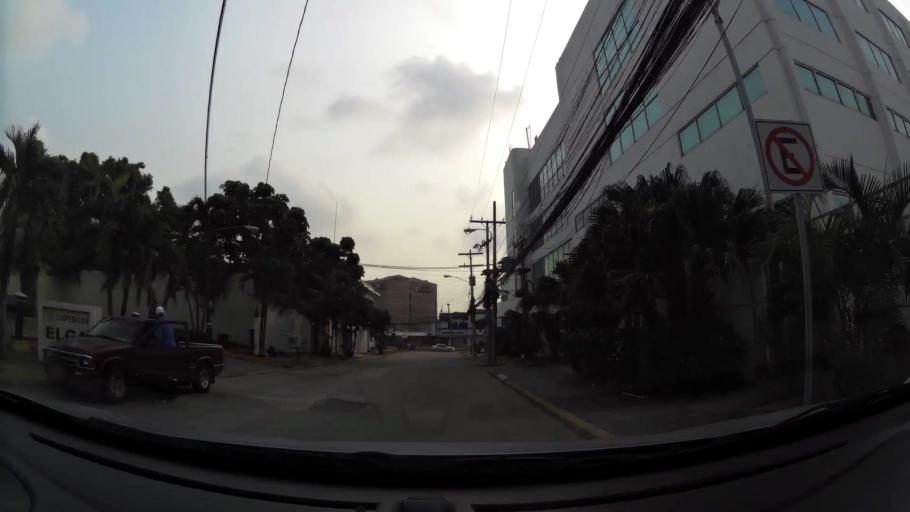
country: HN
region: Cortes
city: Armenta
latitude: 15.4977
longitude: -88.0373
